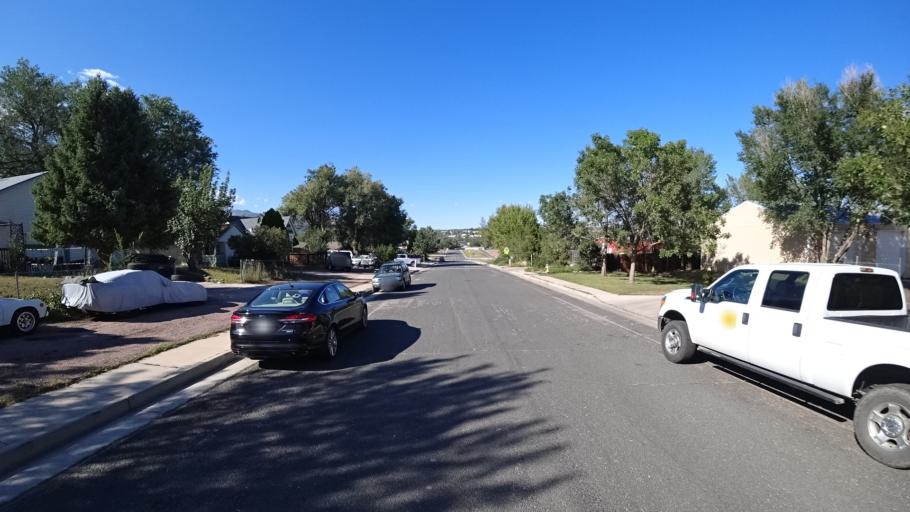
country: US
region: Colorado
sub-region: El Paso County
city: Colorado Springs
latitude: 38.8360
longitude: -104.8644
